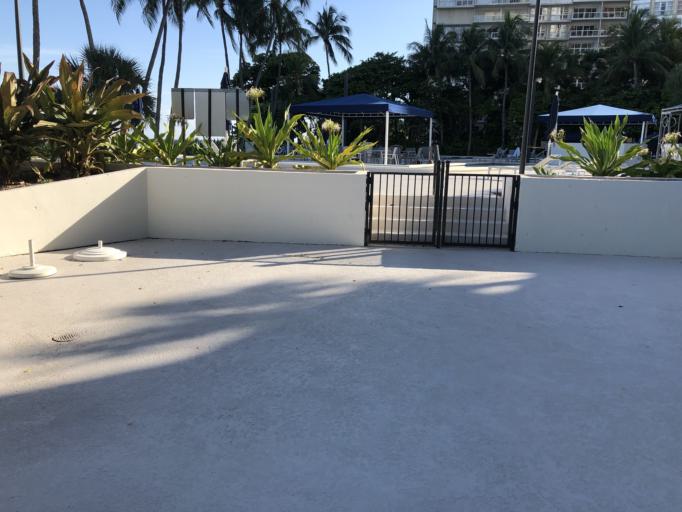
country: US
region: Florida
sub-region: Miami-Dade County
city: Miami
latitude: 25.7505
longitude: -80.1994
